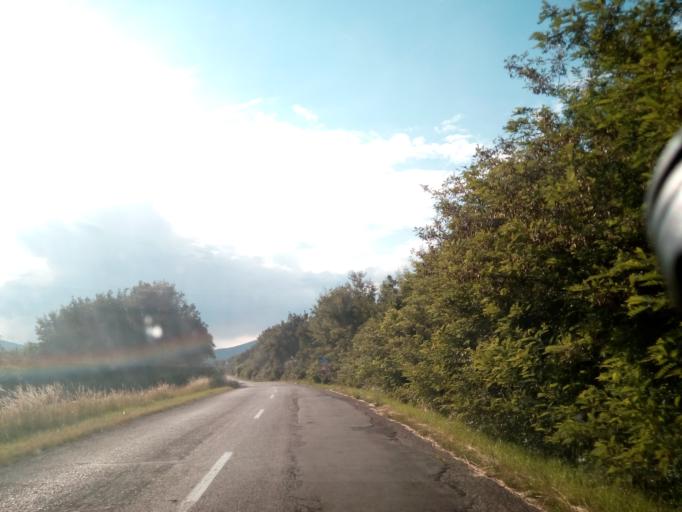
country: SK
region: Kosicky
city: Secovce
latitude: 48.6110
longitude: 21.5485
